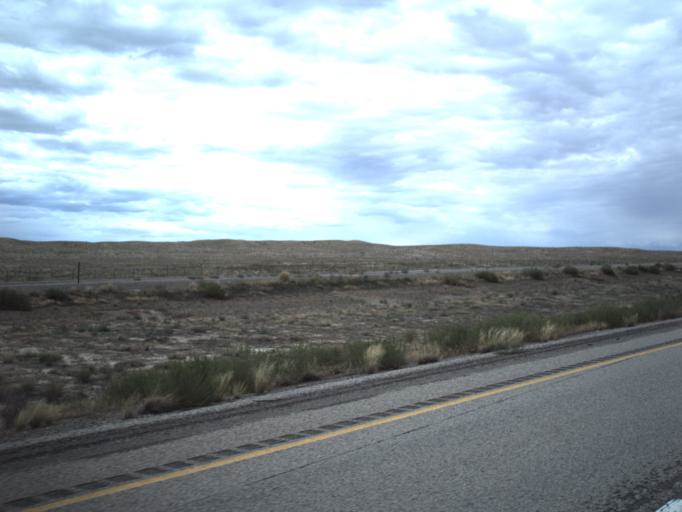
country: US
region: Utah
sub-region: Grand County
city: Moab
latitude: 38.9988
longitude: -109.3222
